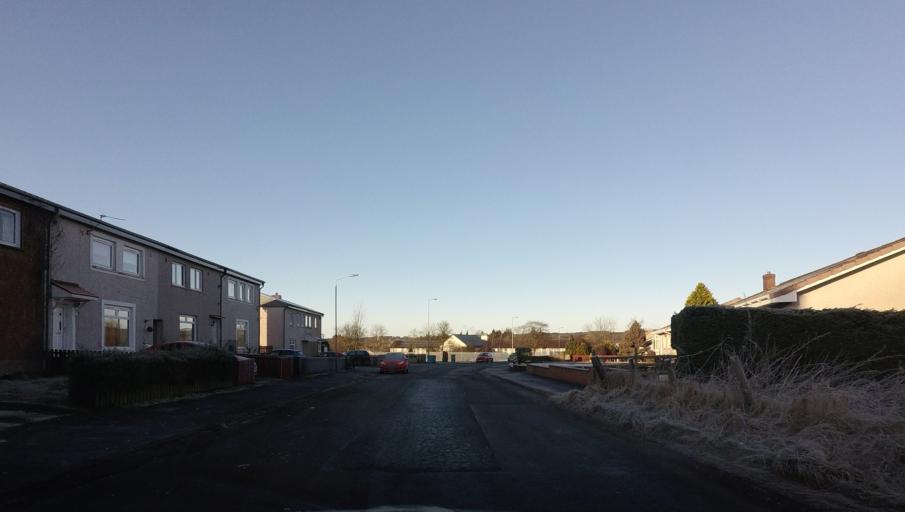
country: GB
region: Scotland
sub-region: North Lanarkshire
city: Shotts
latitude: 55.8004
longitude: -3.8225
